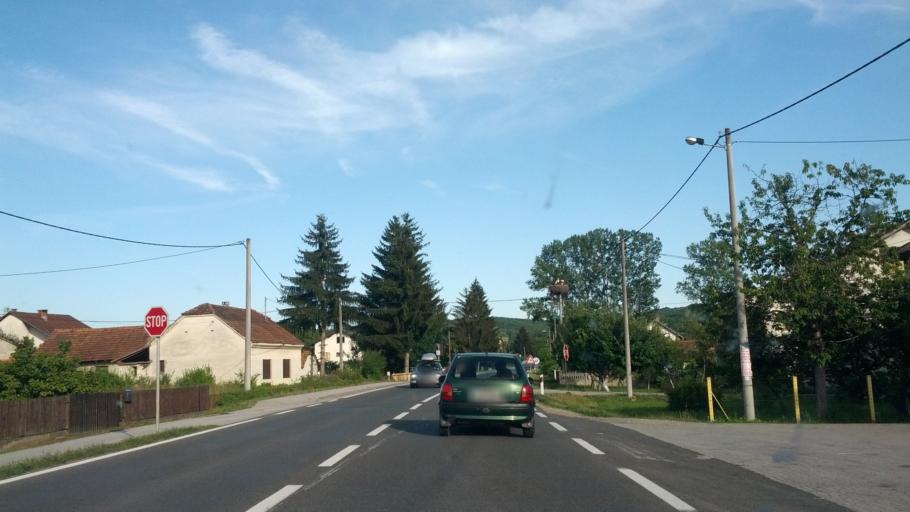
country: HR
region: Karlovacka
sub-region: Grad Karlovac
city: Karlovac
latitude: 45.4310
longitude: 15.6006
